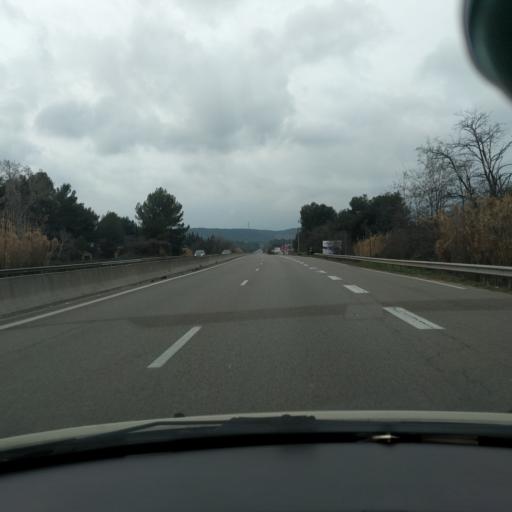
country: FR
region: Provence-Alpes-Cote d'Azur
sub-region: Departement des Bouches-du-Rhone
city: Simiane-Collongue
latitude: 43.4456
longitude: 5.4400
